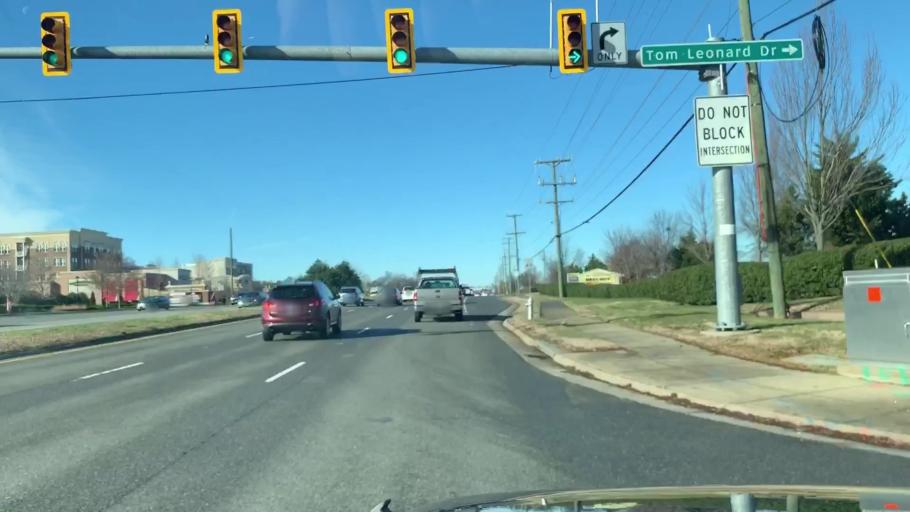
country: US
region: Virginia
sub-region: Henrico County
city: Short Pump
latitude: 37.6492
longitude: -77.6002
